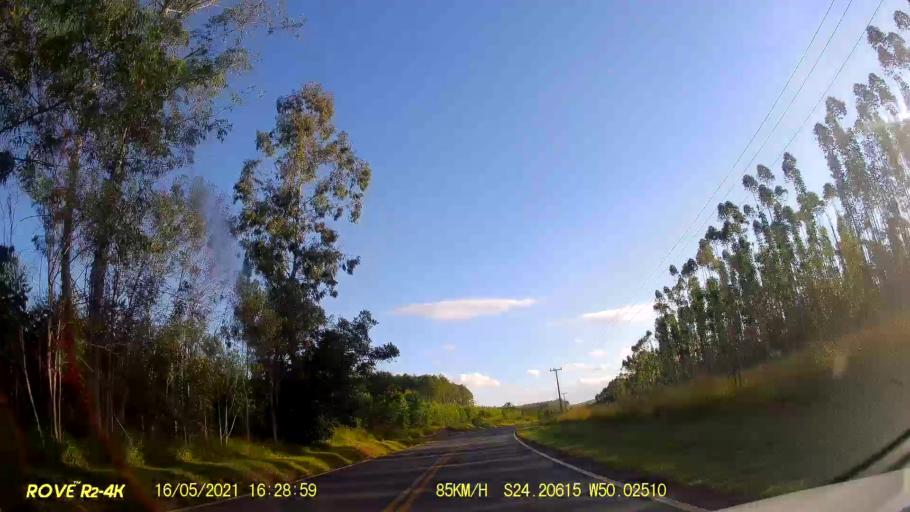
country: BR
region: Parana
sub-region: Jaguariaiva
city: Jaguariaiva
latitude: -24.2063
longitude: -50.0252
